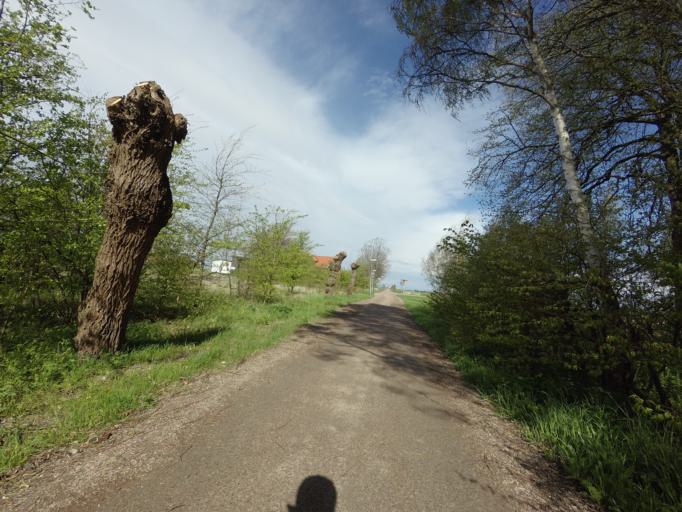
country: SE
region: Skane
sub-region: Malmo
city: Tygelsjo
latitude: 55.5270
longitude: 12.9849
